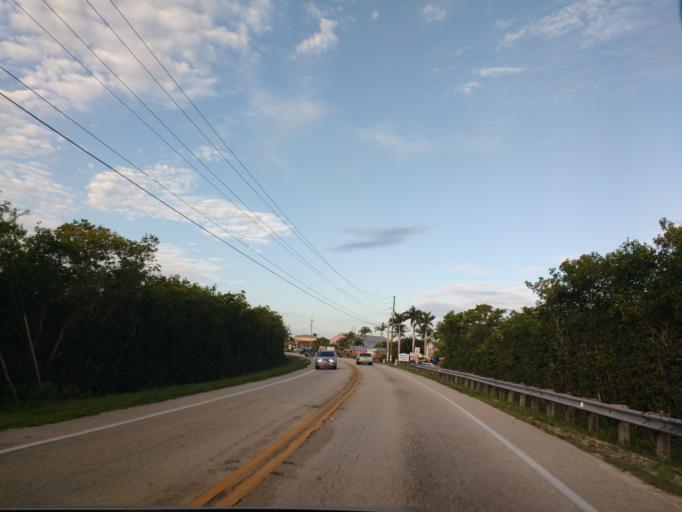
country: US
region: Florida
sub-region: Lee County
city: Pine Island Center
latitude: 26.6367
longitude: -82.0637
